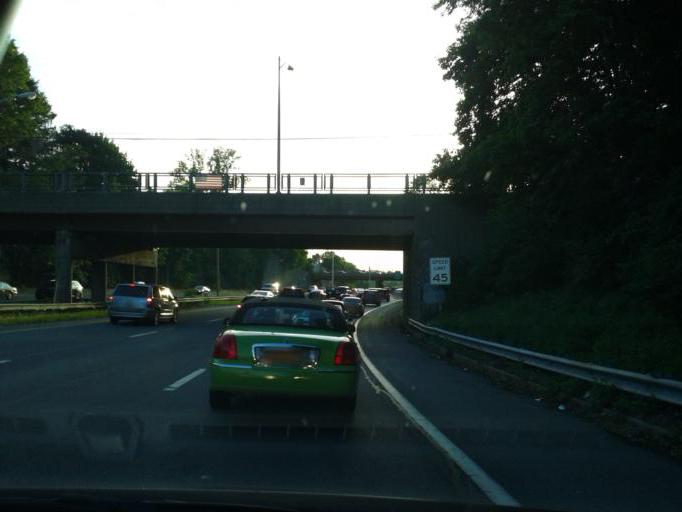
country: US
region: New York
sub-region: Westchester County
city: Bronxville
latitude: 40.9260
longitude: -73.8327
